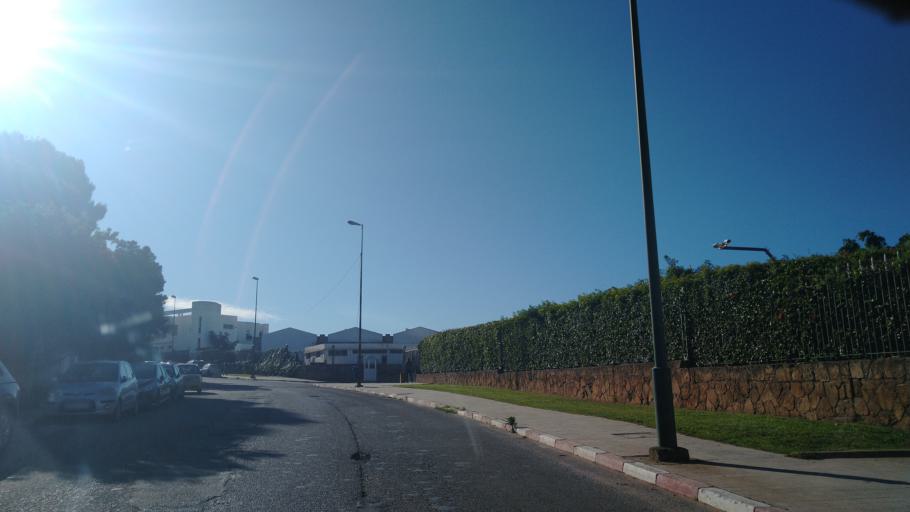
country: MA
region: Rabat-Sale-Zemmour-Zaer
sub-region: Rabat
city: Rabat
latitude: 33.9936
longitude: -6.8595
